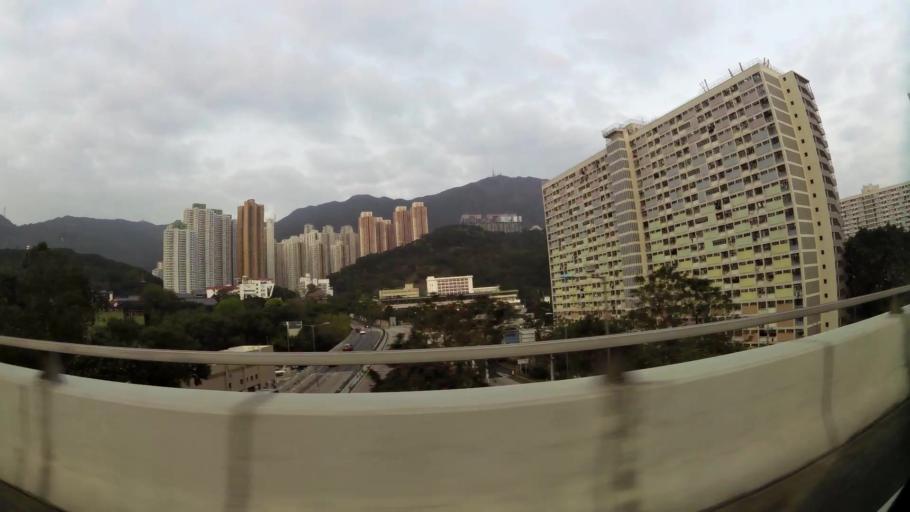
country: HK
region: Wong Tai Sin
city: Wong Tai Sin
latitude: 22.3373
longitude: 114.2038
